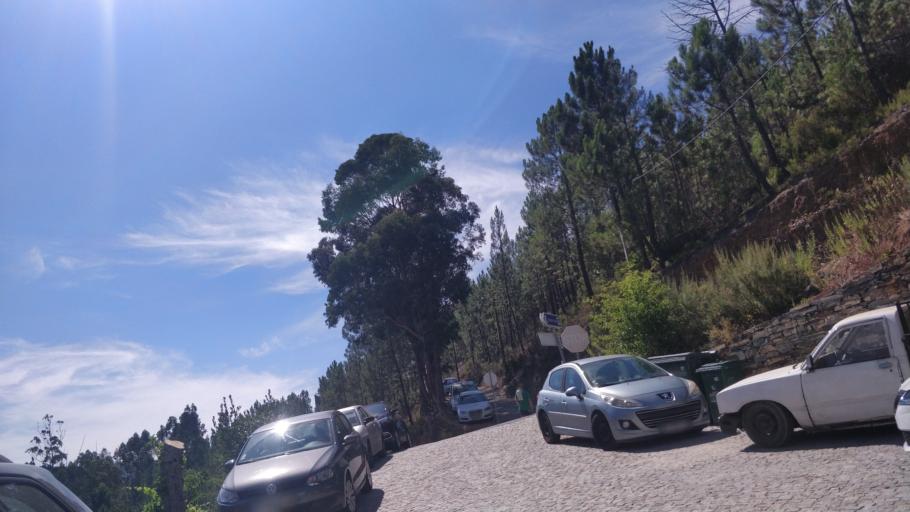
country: PT
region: Guarda
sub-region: Seia
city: Seia
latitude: 40.2861
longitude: -7.7225
